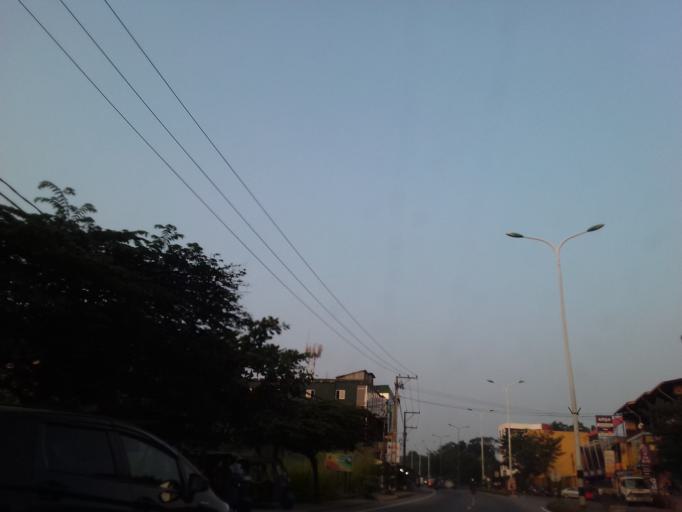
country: LK
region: Western
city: Kelaniya
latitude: 6.9874
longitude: 79.9367
